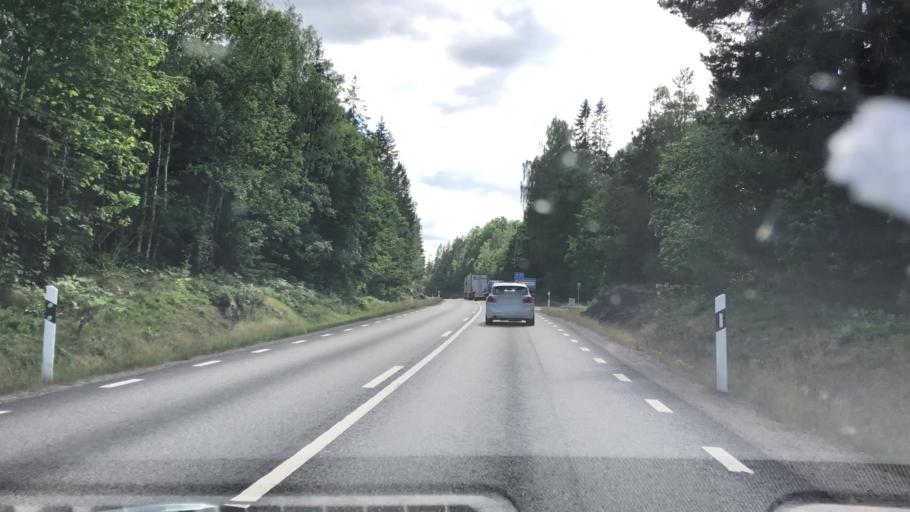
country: SE
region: Kalmar
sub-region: Hultsfreds Kommun
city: Virserum
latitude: 57.2993
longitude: 15.5740
